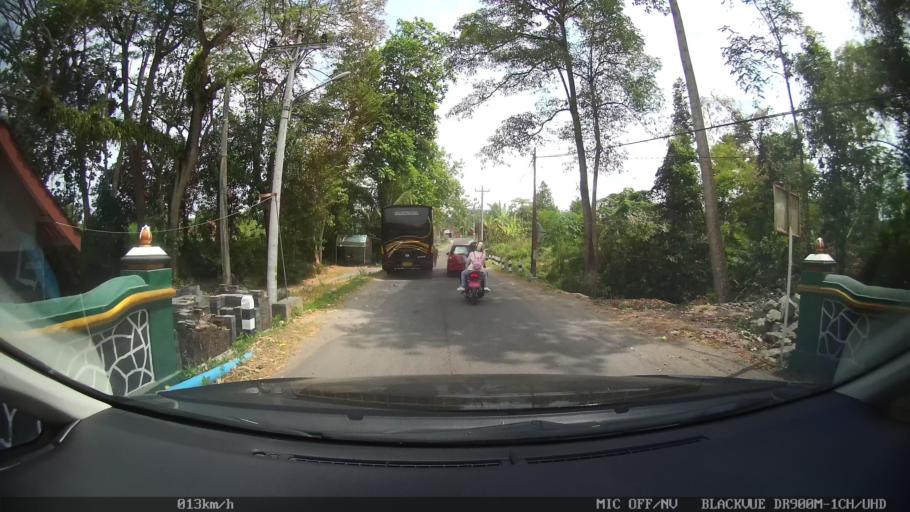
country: ID
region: Central Java
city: Candi Prambanan
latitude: -7.7837
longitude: 110.4905
